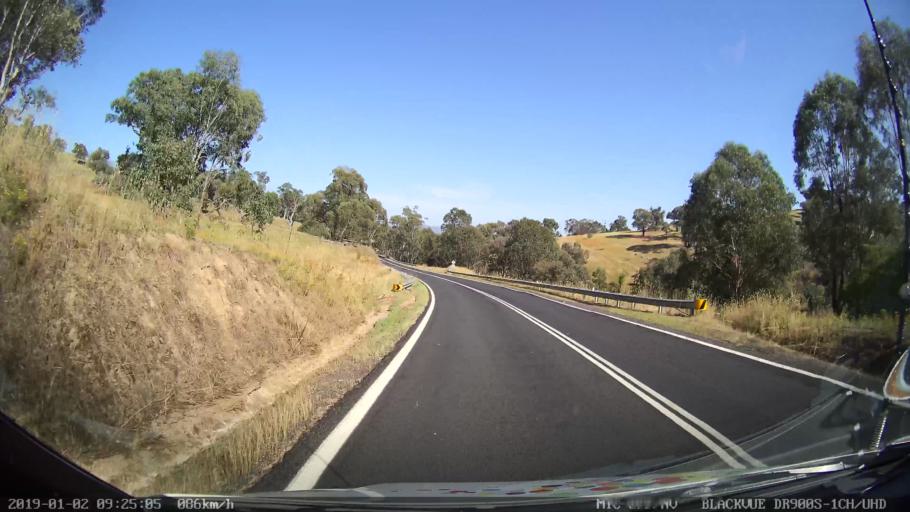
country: AU
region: New South Wales
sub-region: Tumut Shire
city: Tumut
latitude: -35.3687
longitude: 148.2911
